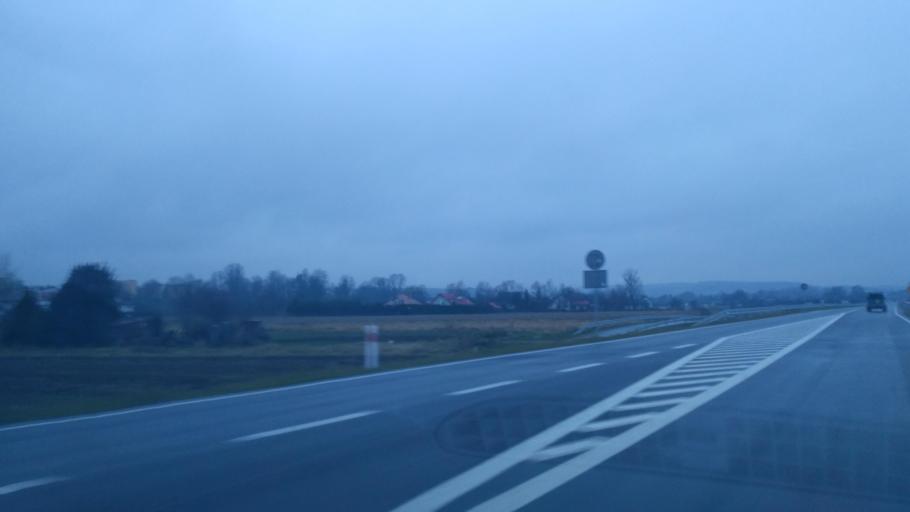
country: PL
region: Subcarpathian Voivodeship
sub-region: Powiat rzeszowski
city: Dynow
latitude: 49.8158
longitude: 22.2407
